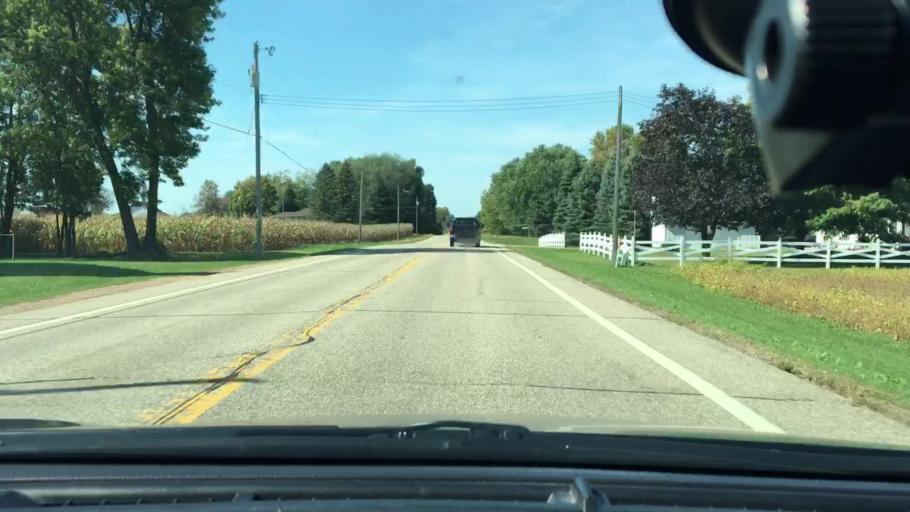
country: US
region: Minnesota
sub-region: Wright County
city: Hanover
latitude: 45.1236
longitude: -93.6252
